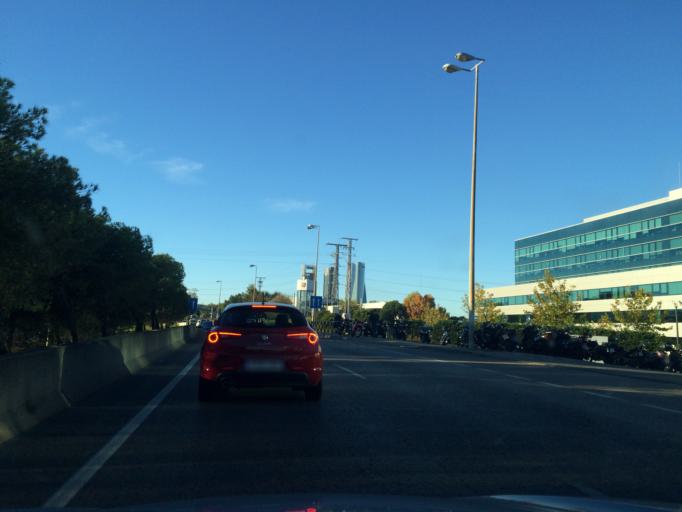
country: ES
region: Madrid
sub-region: Provincia de Madrid
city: Pinar de Chamartin
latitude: 40.4917
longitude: -3.6719
